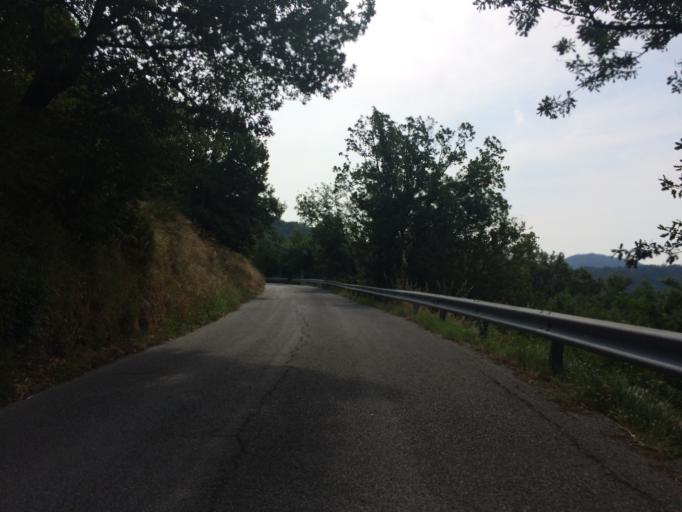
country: IT
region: Liguria
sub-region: Provincia di Savona
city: San Giovanni
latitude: 44.3940
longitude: 8.5053
